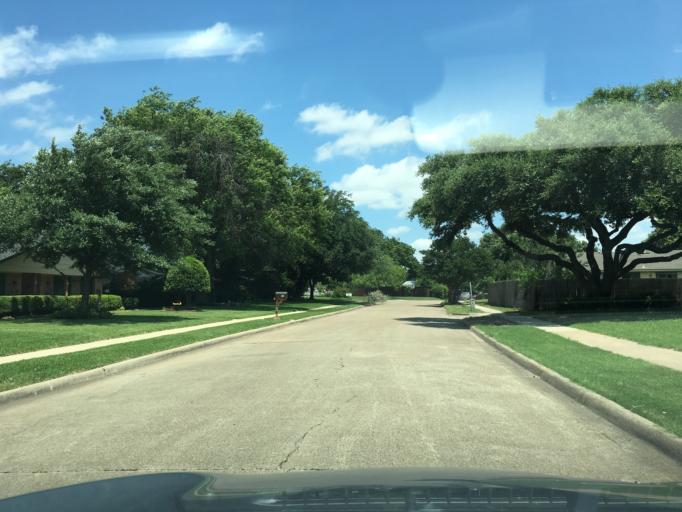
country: US
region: Texas
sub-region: Dallas County
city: Richardson
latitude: 32.9622
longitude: -96.6906
